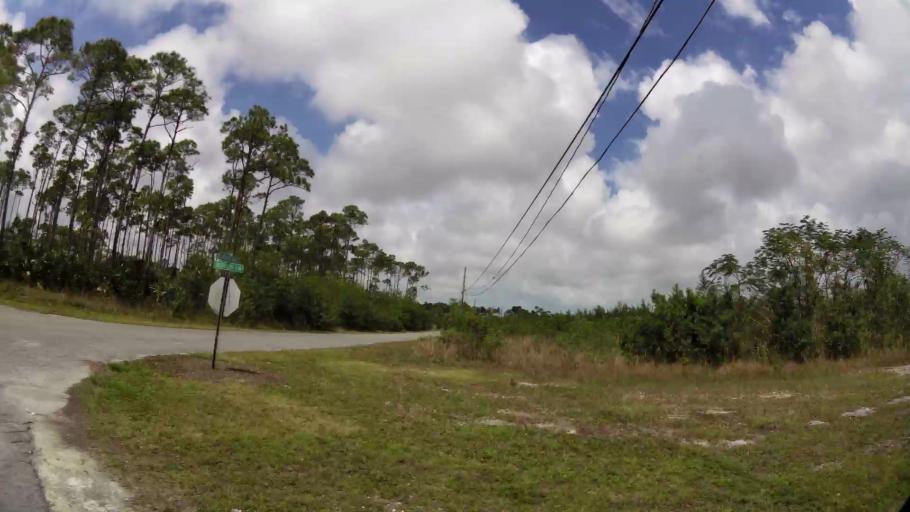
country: BS
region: Freeport
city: Lucaya
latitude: 26.5310
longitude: -78.6543
